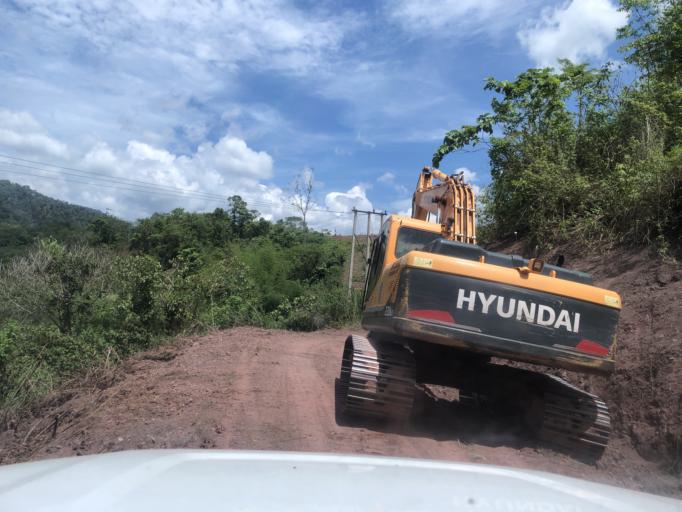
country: CN
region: Yunnan
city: Menglie
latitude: 22.2407
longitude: 101.6160
